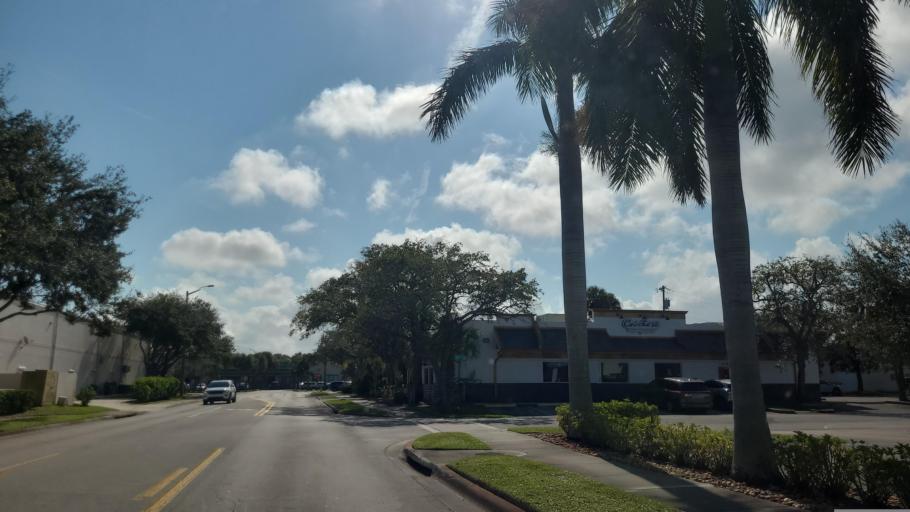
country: US
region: Florida
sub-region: Indian River County
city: Vero Beach
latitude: 27.6410
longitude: -80.3871
